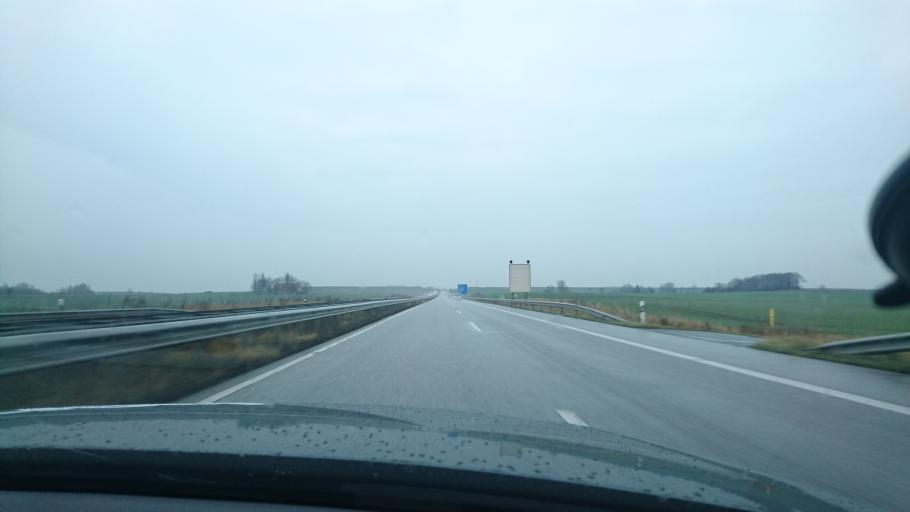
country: DE
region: Schleswig-Holstein
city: Gremersdorf
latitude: 54.3512
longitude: 10.9529
